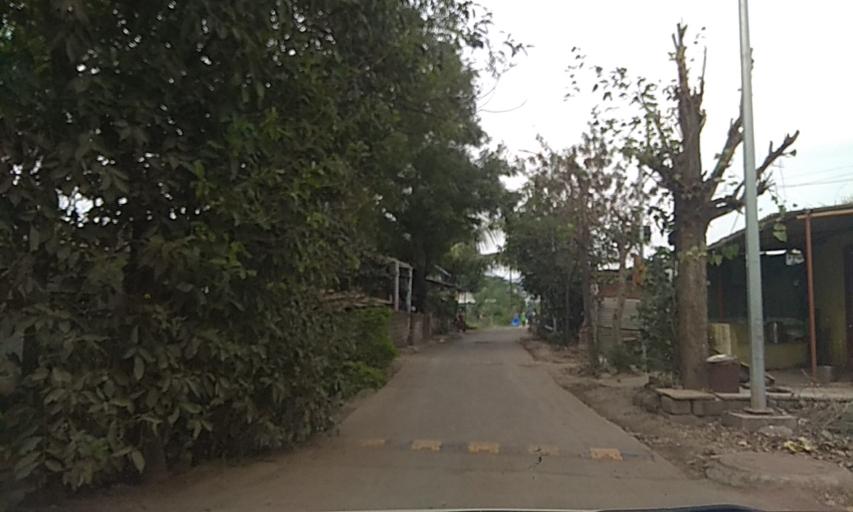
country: IN
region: Maharashtra
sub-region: Pune Division
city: Pimpri
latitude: 18.5773
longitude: 73.7086
